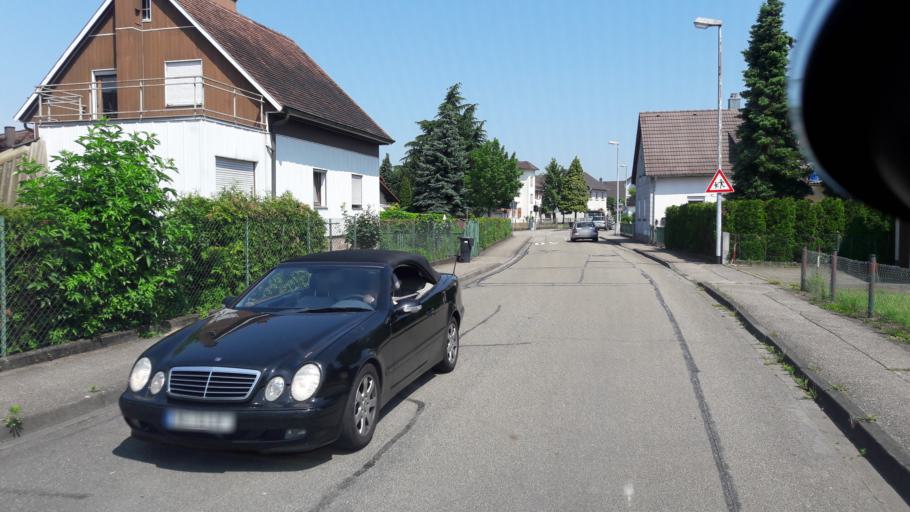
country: DE
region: Baden-Wuerttemberg
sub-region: Karlsruhe Region
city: Kuppenheim
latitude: 48.8548
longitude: 8.2477
